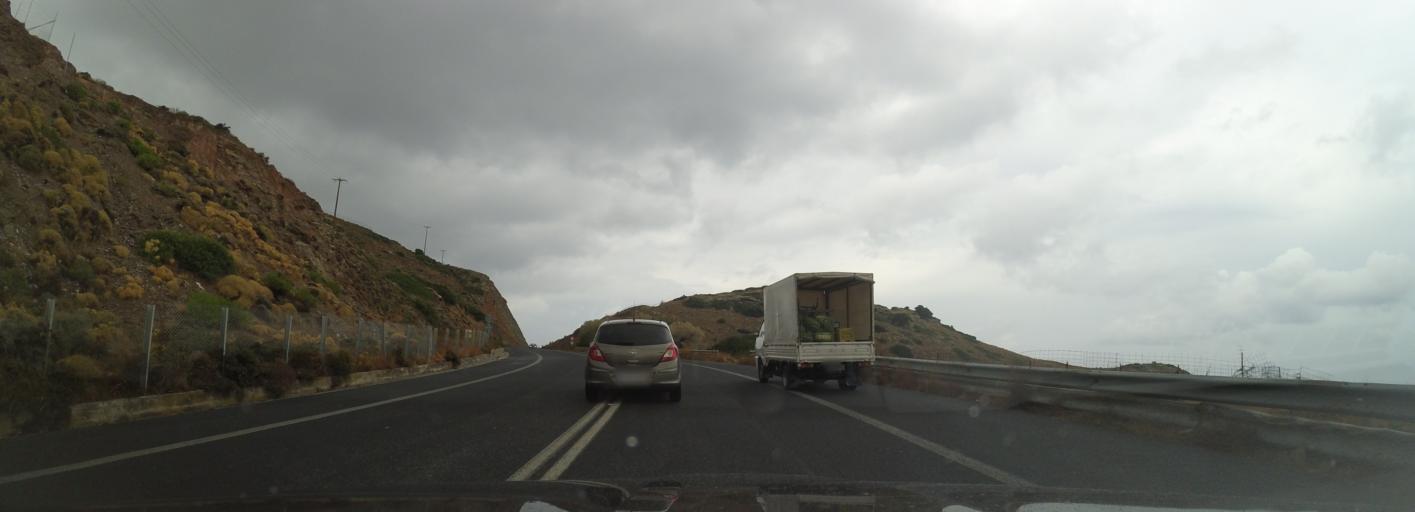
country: GR
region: Crete
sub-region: Nomos Irakleiou
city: Gazi
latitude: 35.3884
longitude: 25.0366
